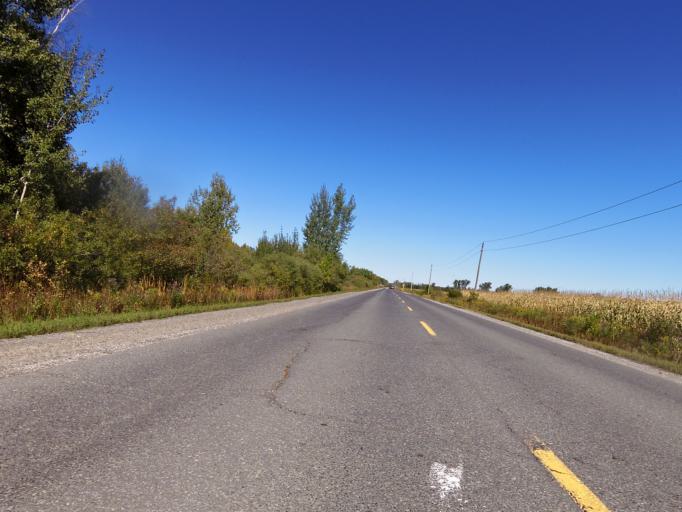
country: CA
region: Ontario
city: Clarence-Rockland
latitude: 45.3290
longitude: -75.4158
